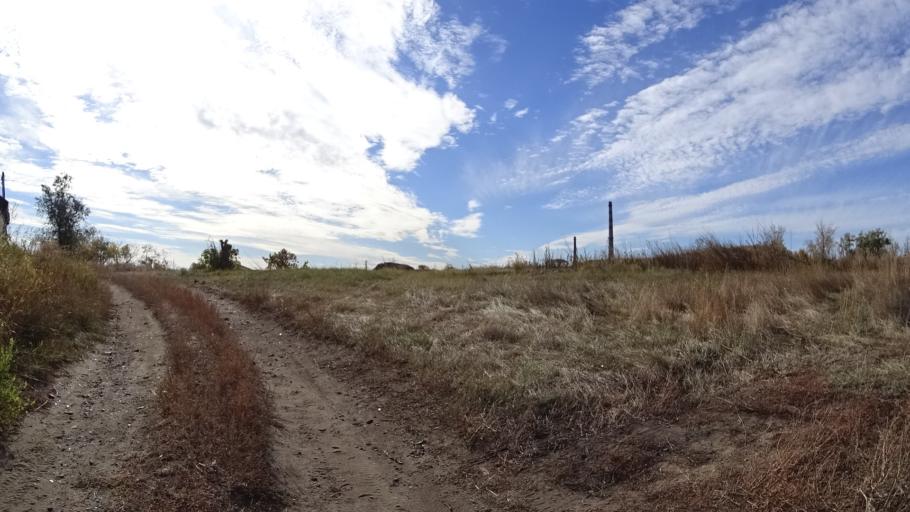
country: RU
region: Chelyabinsk
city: Troitsk
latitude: 54.0746
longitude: 61.5797
